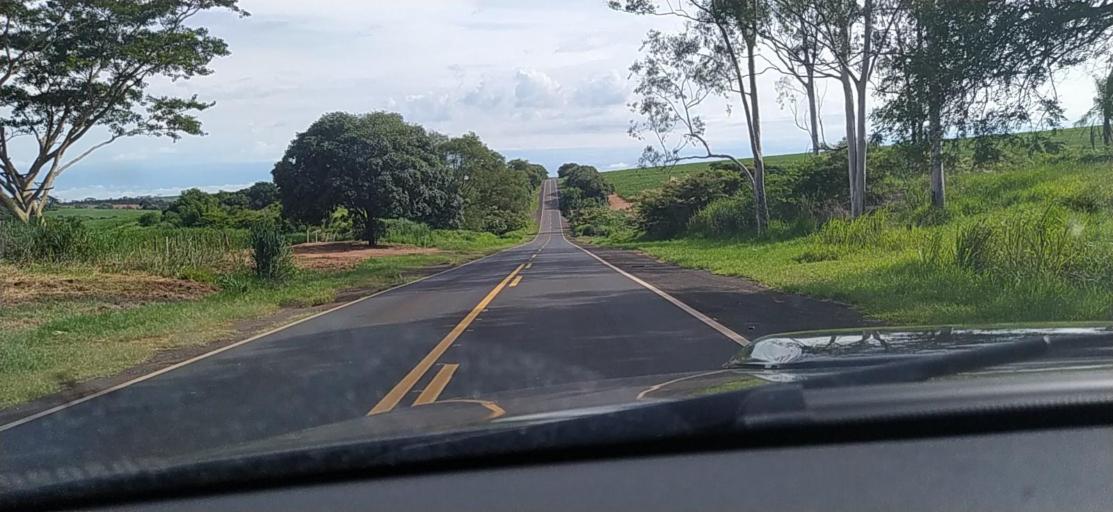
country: BR
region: Sao Paulo
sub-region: Catanduva
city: Catanduva
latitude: -21.0852
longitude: -49.0737
